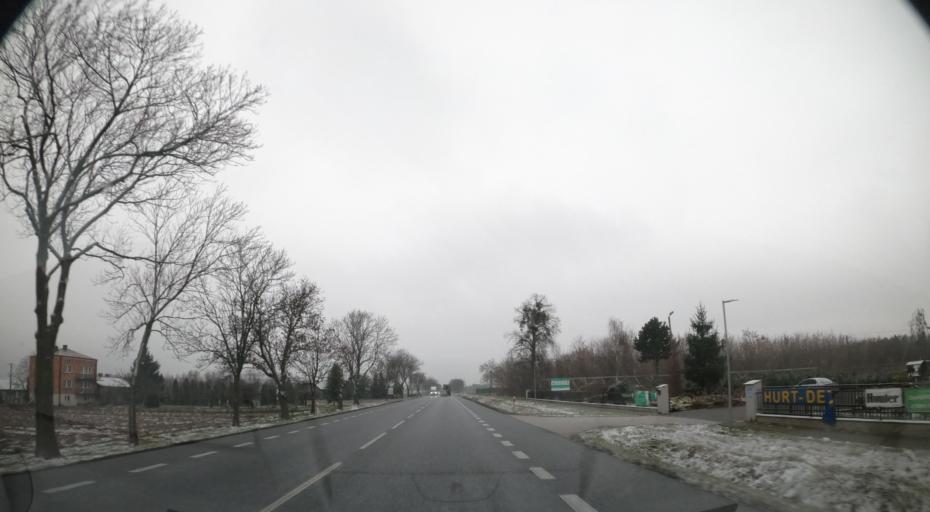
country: PL
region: Masovian Voivodeship
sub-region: Powiat sochaczewski
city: Sochaczew
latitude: 52.2234
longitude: 20.3049
